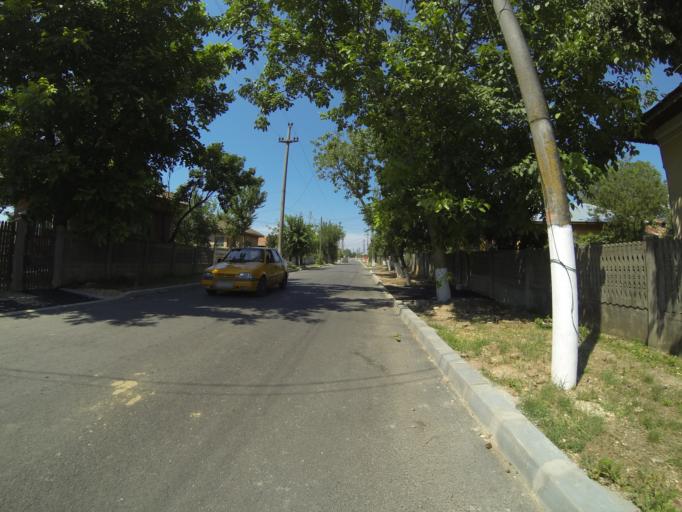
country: RO
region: Dolj
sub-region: Comuna Segarcea
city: Segarcea
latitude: 44.0955
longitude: 23.7343
